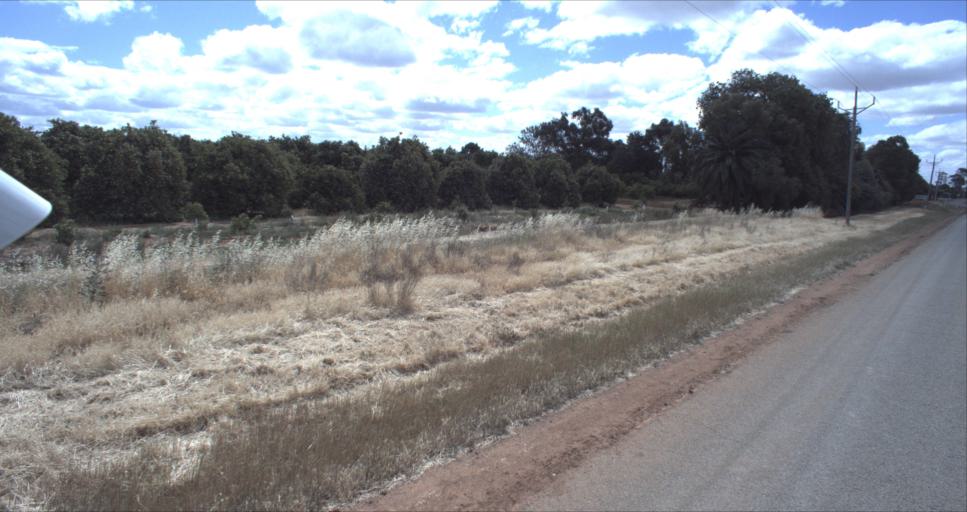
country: AU
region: New South Wales
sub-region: Leeton
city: Leeton
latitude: -34.5834
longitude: 146.3965
